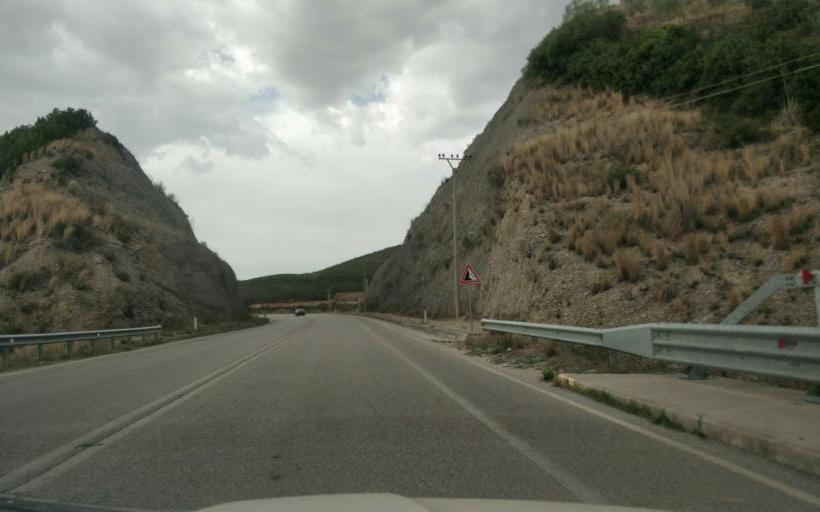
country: AL
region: Vlore
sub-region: Rrethi i Vlores
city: Selenice
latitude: 40.5566
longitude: 19.6530
